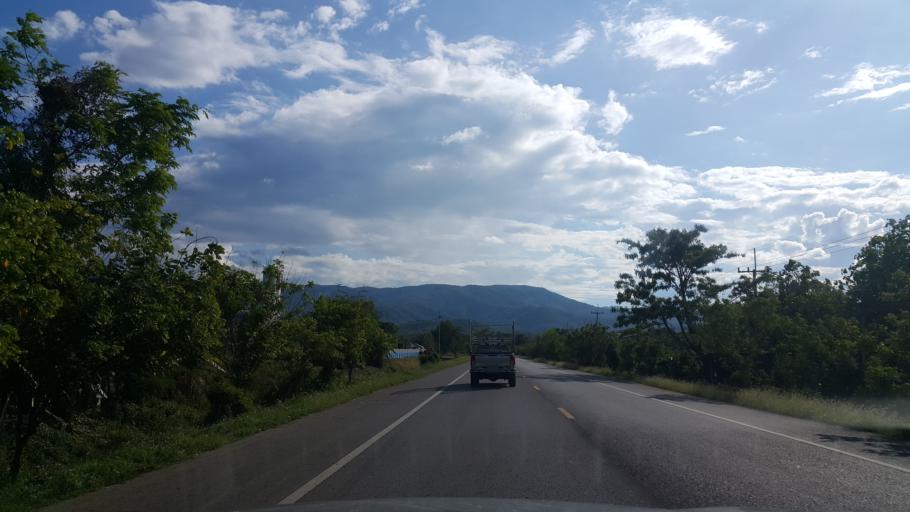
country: TH
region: Phayao
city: Phayao
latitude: 19.0813
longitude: 99.8737
